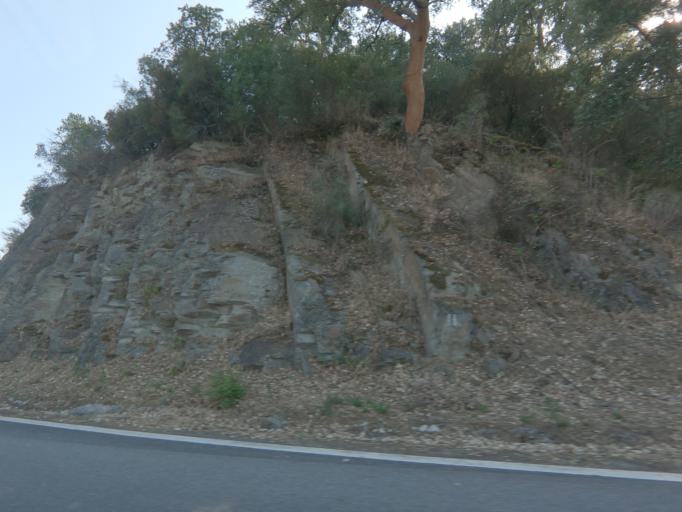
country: PT
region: Viseu
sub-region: Tabuaco
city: Tabuaco
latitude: 41.1396
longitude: -7.5636
